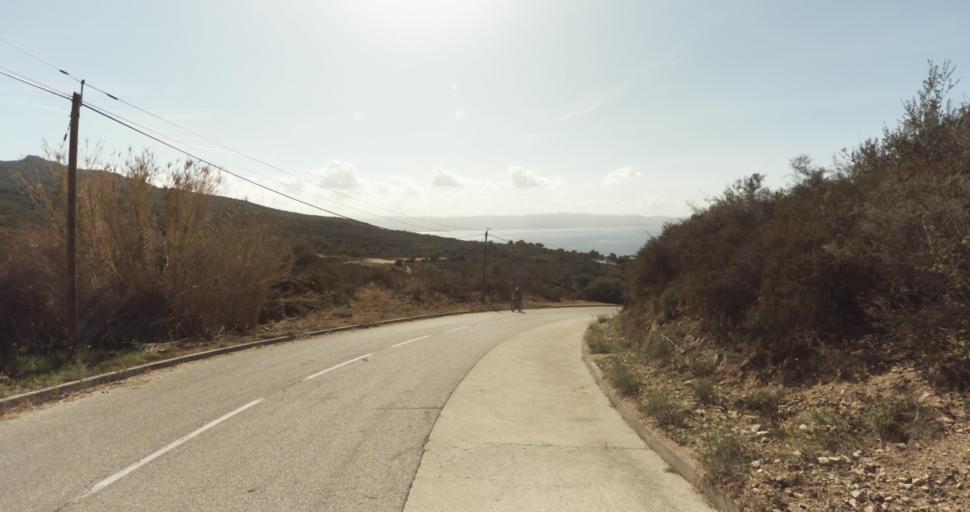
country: FR
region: Corsica
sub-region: Departement de la Corse-du-Sud
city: Ajaccio
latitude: 41.9158
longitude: 8.6439
